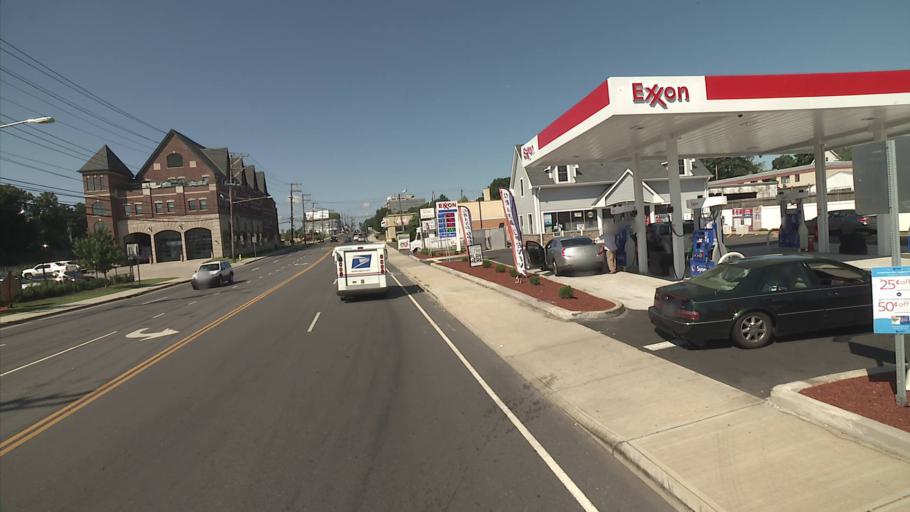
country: US
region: Connecticut
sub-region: Fairfield County
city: Norwalk
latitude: 41.1062
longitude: -73.4263
